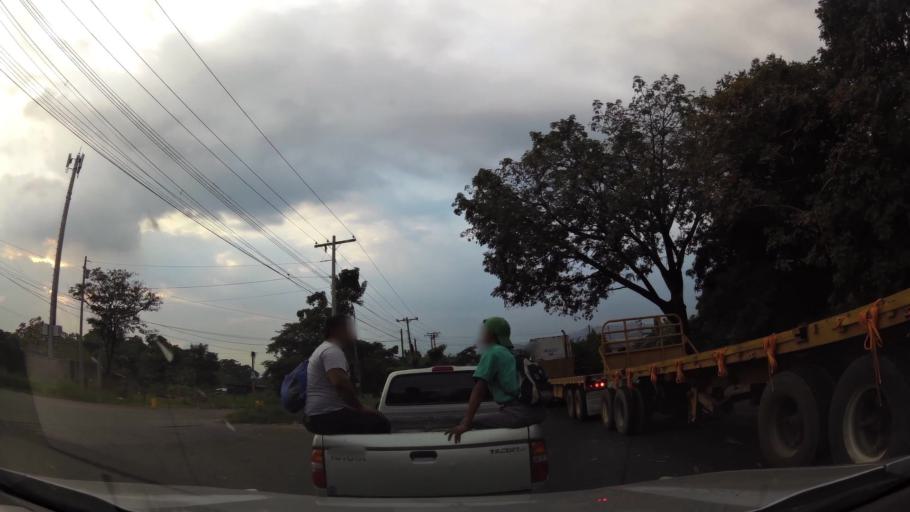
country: GT
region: Escuintla
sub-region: Municipio de Escuintla
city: Escuintla
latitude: 14.2829
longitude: -90.7882
